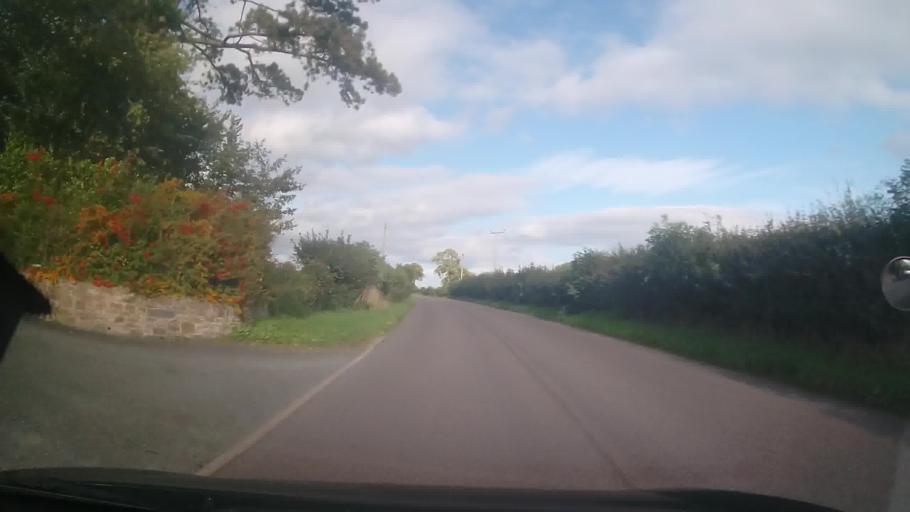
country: GB
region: England
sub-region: Shropshire
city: Craven Arms
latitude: 52.4297
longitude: -2.8846
